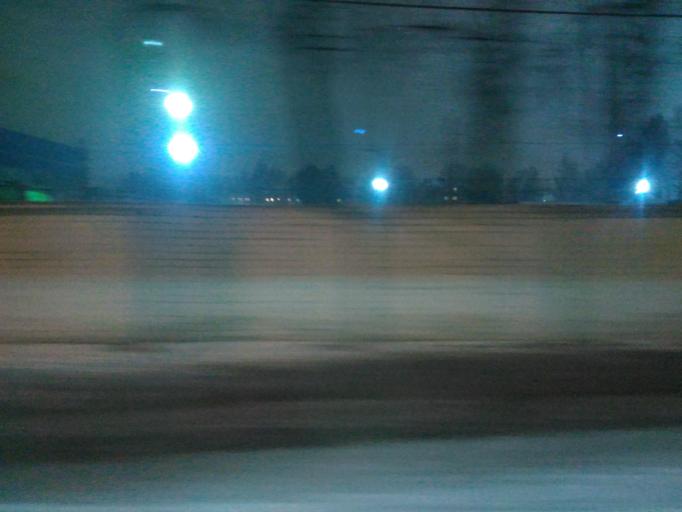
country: RU
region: Ulyanovsk
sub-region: Ulyanovskiy Rayon
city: Ulyanovsk
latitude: 54.3438
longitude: 48.3933
